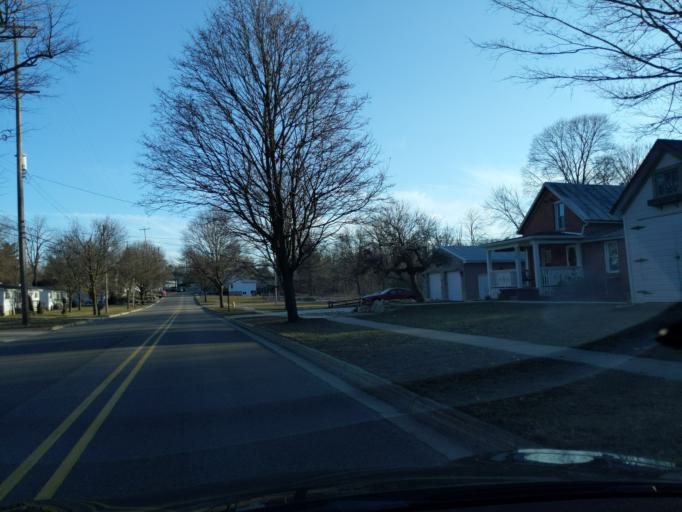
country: US
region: Michigan
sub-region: Ingham County
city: Mason
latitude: 42.5853
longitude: -84.4431
